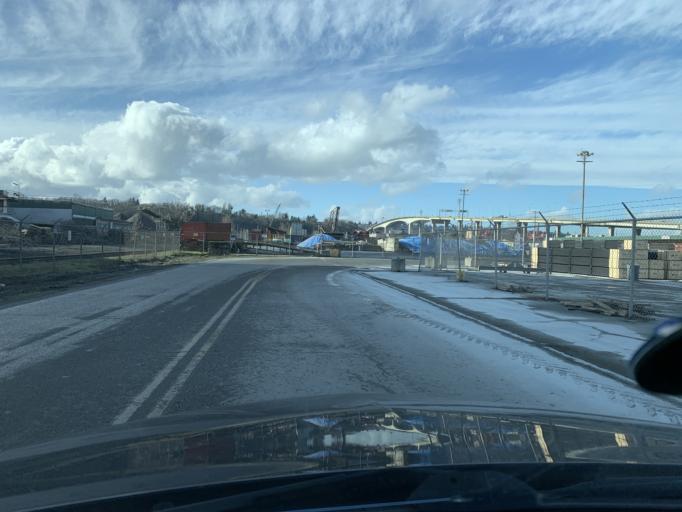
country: US
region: Washington
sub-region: King County
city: Seattle
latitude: 47.5693
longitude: -122.3422
